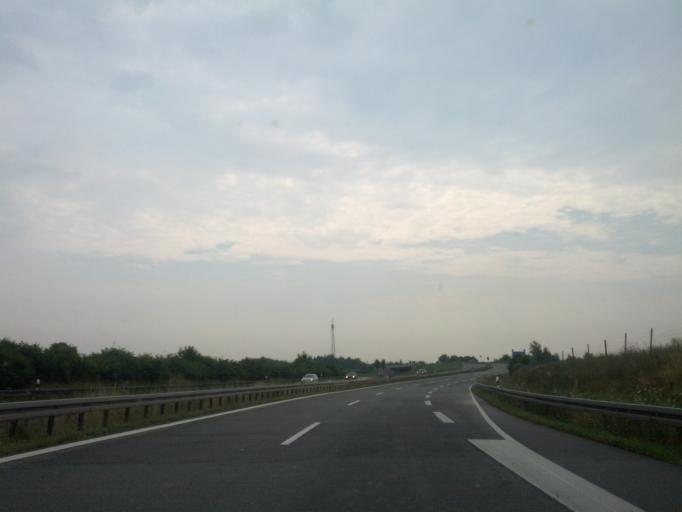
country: DE
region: Mecklenburg-Vorpommern
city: Kritzmow
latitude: 54.0210
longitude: 12.0593
